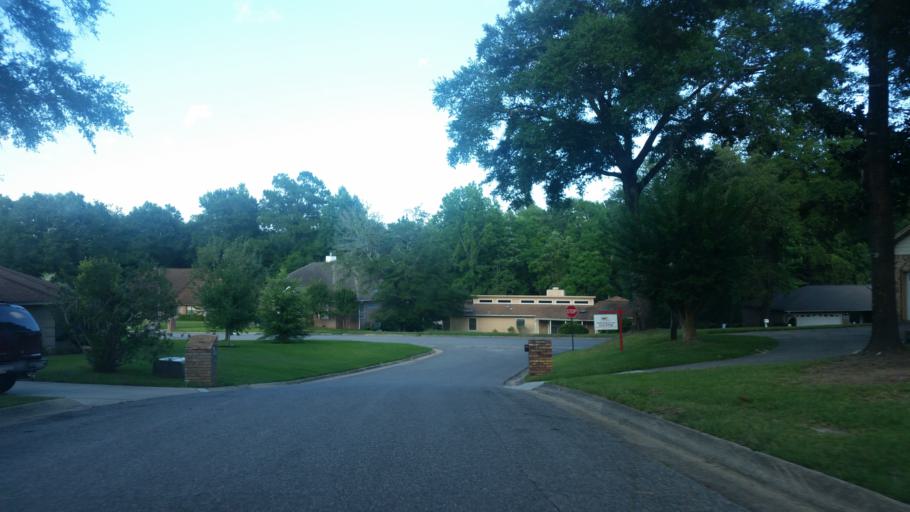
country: US
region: Florida
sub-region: Escambia County
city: Ferry Pass
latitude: 30.5103
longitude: -87.1677
